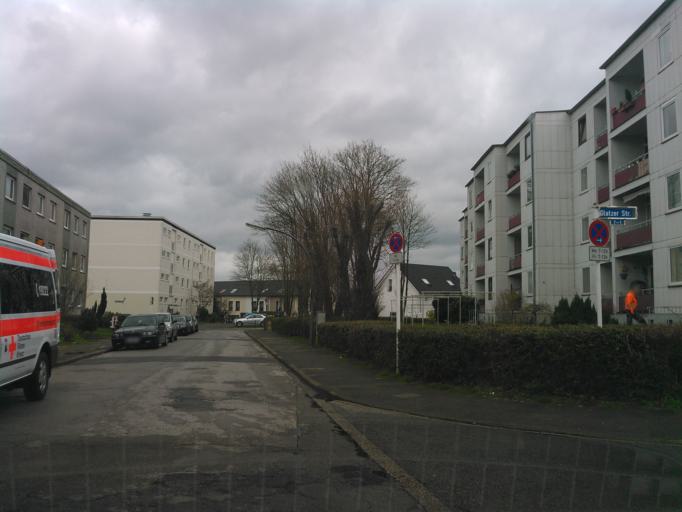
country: DE
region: North Rhine-Westphalia
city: Marl
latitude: 51.6490
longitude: 7.0926
